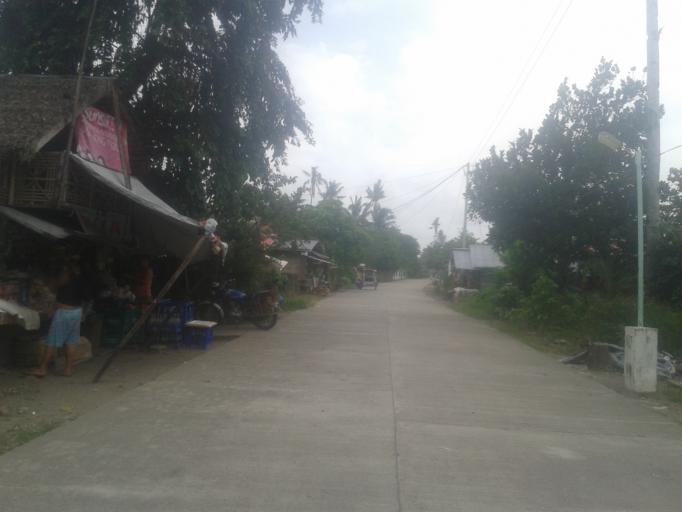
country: PH
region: Eastern Visayas
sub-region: Province of Leyte
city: Mayorga
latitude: 10.8910
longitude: 125.0105
